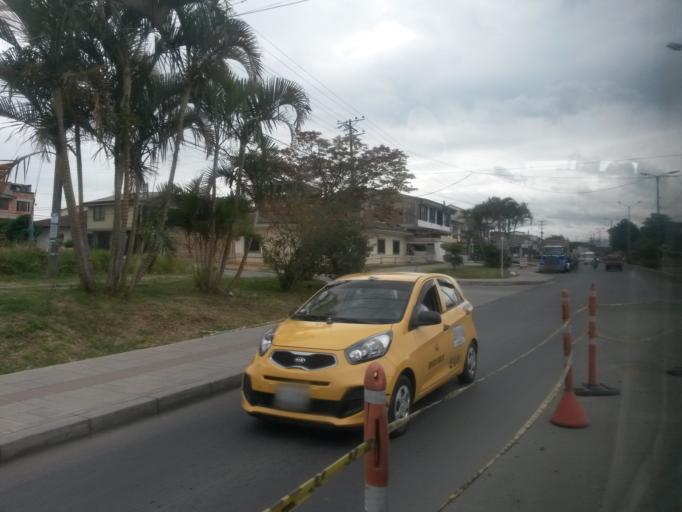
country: CO
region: Cauca
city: Popayan
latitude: 2.4544
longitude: -76.5932
